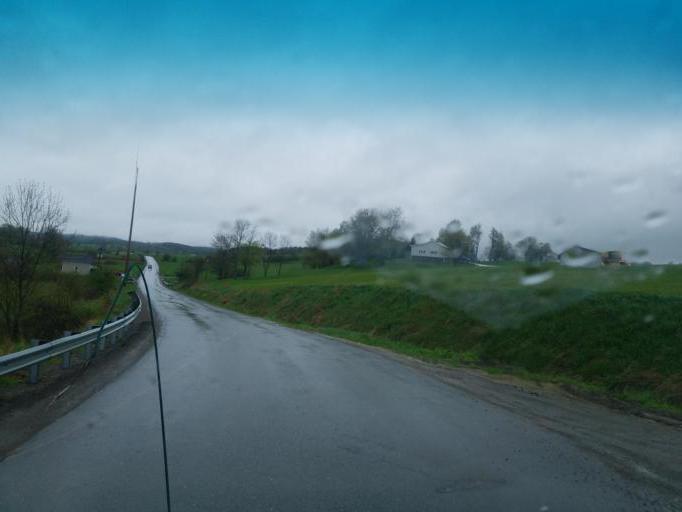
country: US
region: Pennsylvania
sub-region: Tioga County
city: Westfield
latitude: 41.9620
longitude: -77.6478
